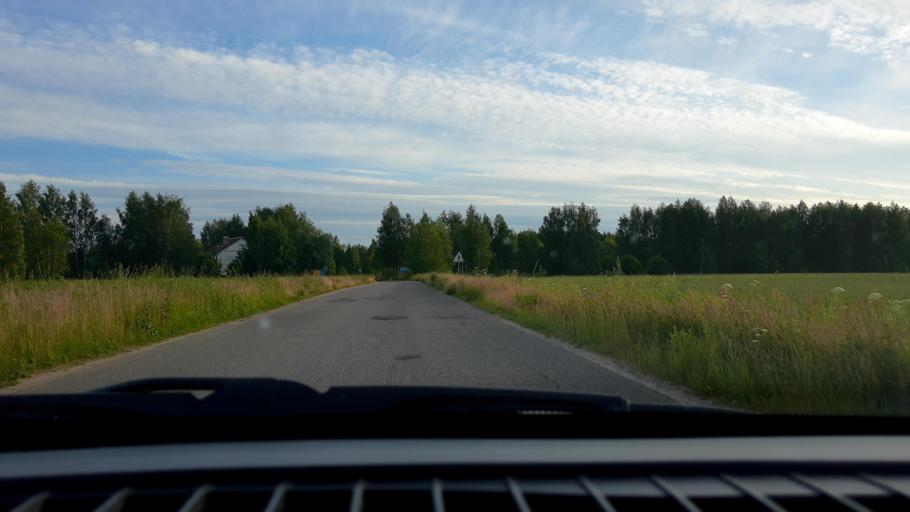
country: RU
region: Nizjnij Novgorod
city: Kstovo
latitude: 56.2623
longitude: 44.3258
